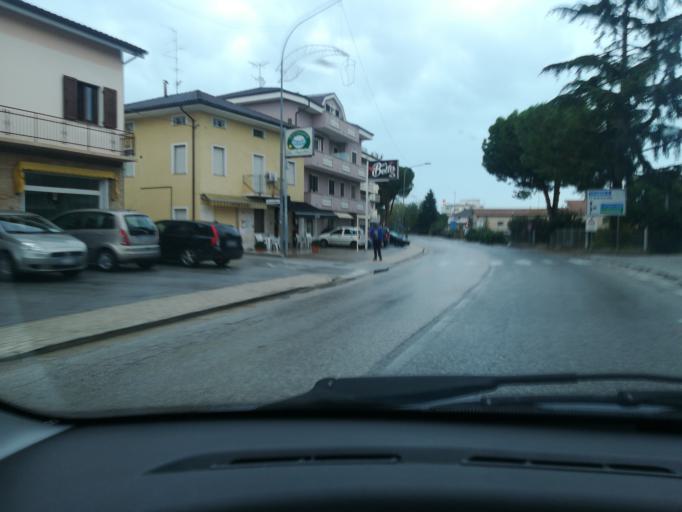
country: IT
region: The Marches
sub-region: Provincia di Macerata
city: Borgo Stazione
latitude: 43.2868
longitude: 13.6483
